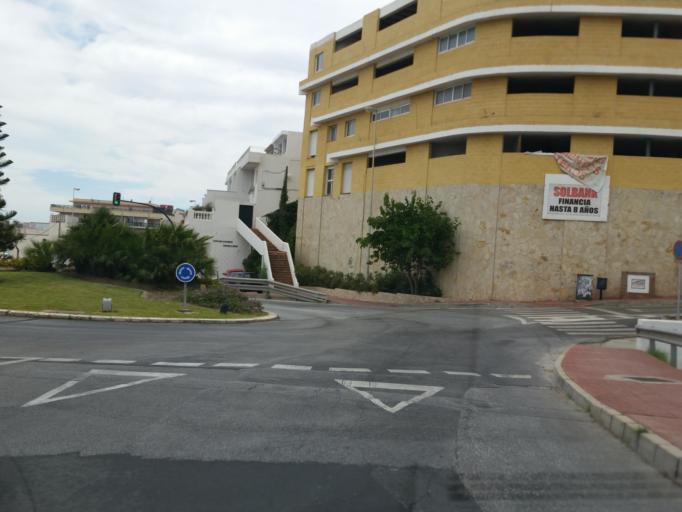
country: ES
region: Andalusia
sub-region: Provincia de Malaga
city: Benalmadena
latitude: 36.5730
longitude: -4.5888
